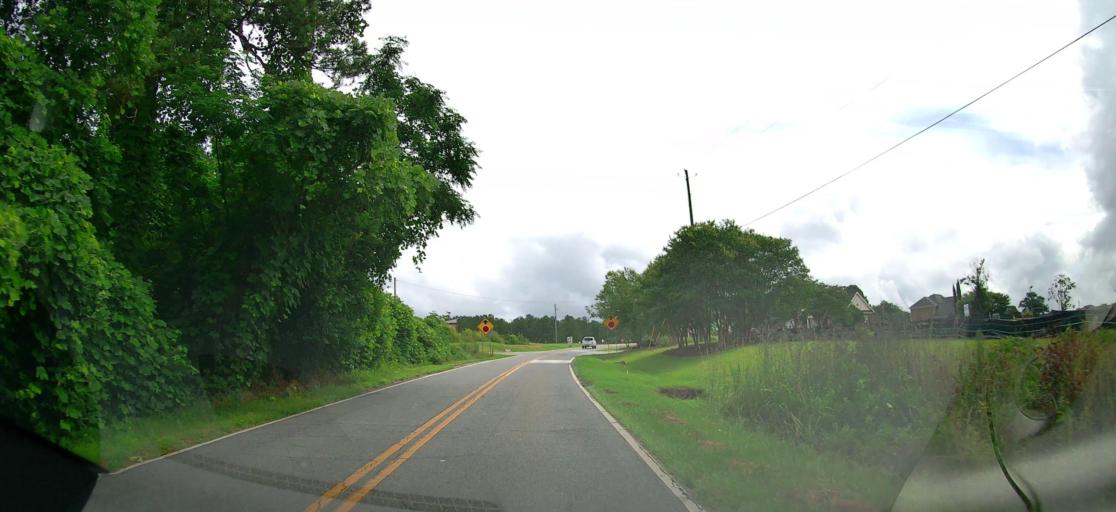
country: US
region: Georgia
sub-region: Bibb County
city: West Point
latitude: 32.7965
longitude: -83.7843
